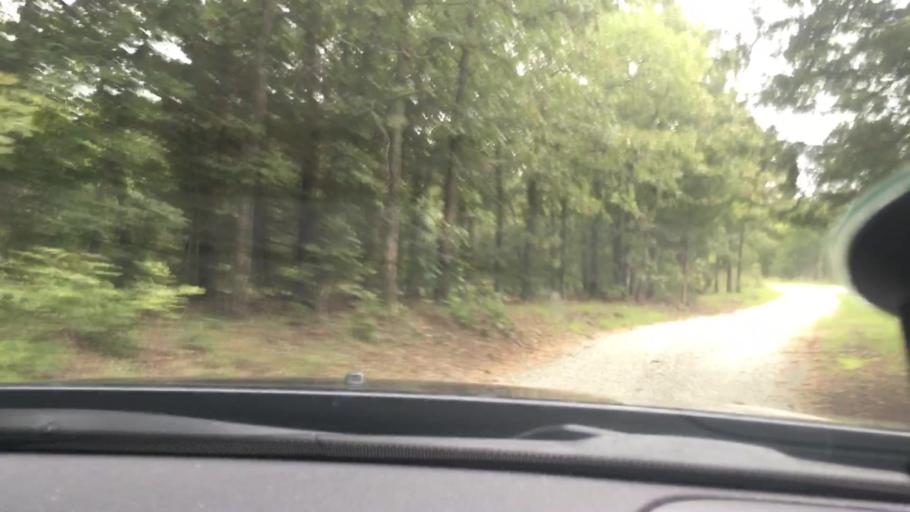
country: US
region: Oklahoma
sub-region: Pontotoc County
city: Byng
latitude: 34.8175
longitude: -96.5339
